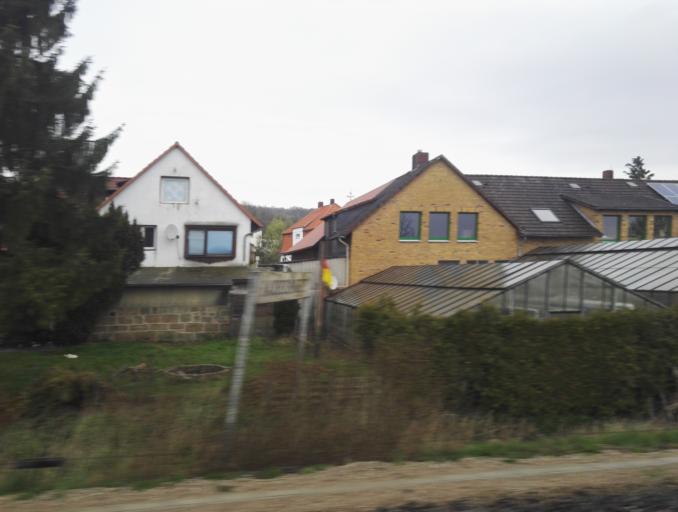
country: DE
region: Lower Saxony
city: Baddeckenstedt
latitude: 52.0875
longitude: 10.2355
